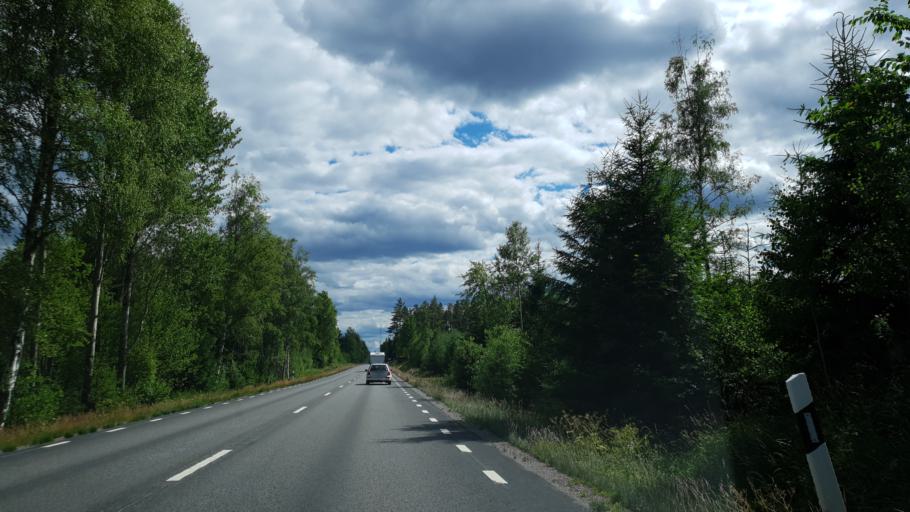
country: SE
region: Kronoberg
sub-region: Lessebo Kommun
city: Lessebo
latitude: 56.7920
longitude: 15.4132
